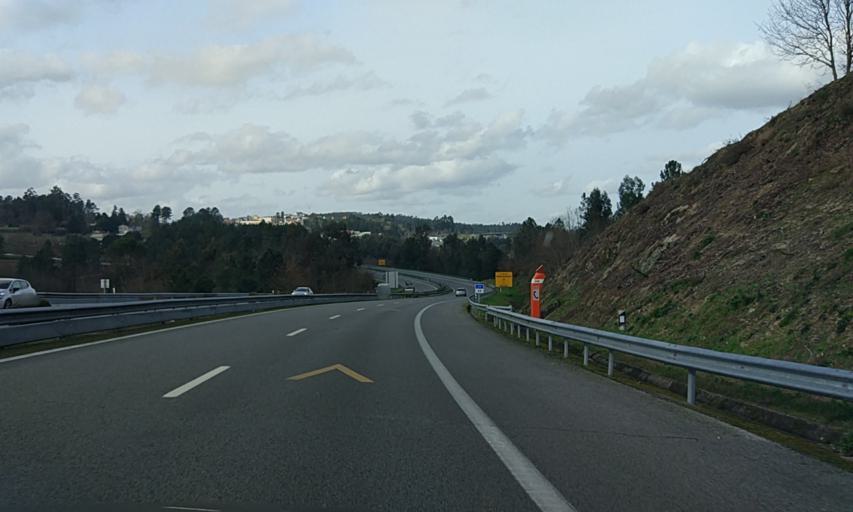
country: PT
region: Porto
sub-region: Marco de Canaveses
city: Marco de Canavezes
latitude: 41.2237
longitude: -8.1666
